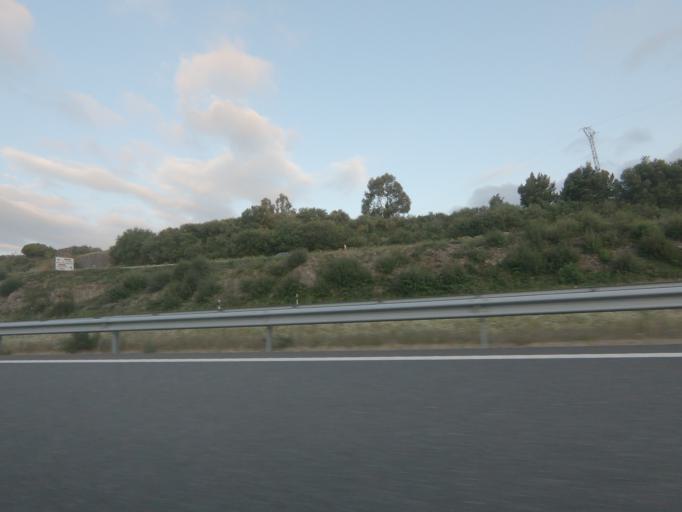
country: ES
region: Galicia
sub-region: Provincia de Ourense
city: Melon
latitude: 42.2051
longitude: -8.2692
